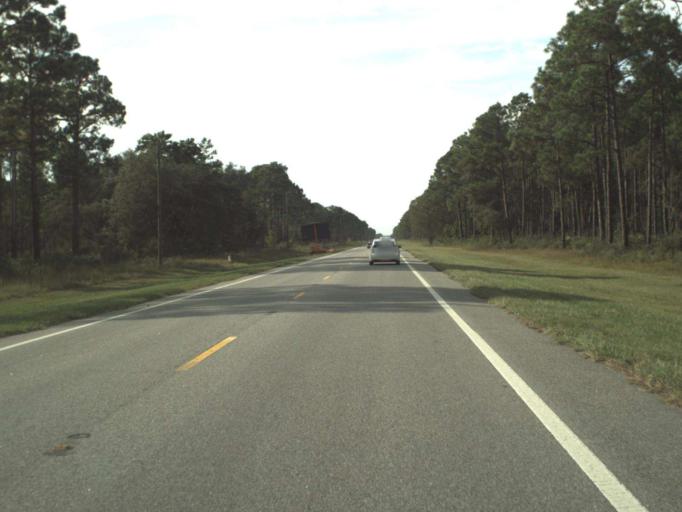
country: US
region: Florida
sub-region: Bay County
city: Mexico Beach
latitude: 30.0051
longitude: -85.5061
